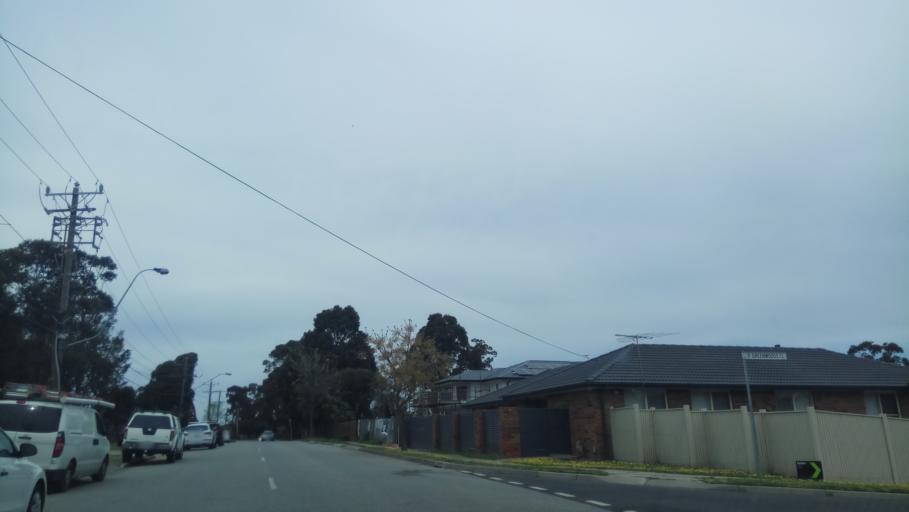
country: AU
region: Victoria
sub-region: Kingston
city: Dingley Village
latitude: -37.9735
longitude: 145.1333
